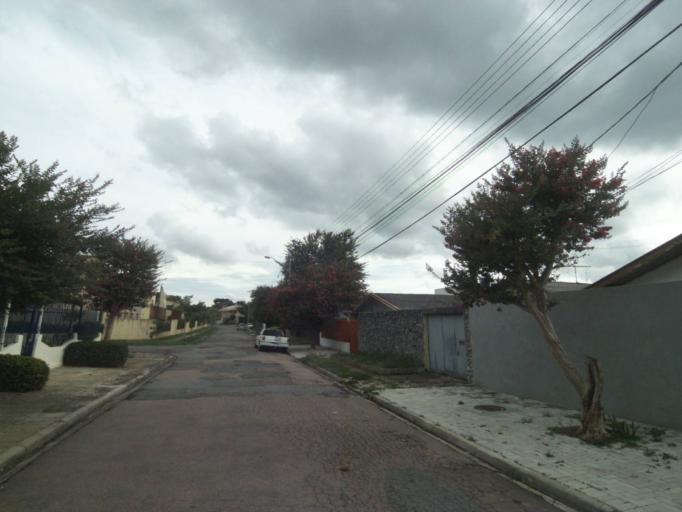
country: BR
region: Parana
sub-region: Curitiba
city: Curitiba
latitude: -25.4420
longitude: -49.3151
